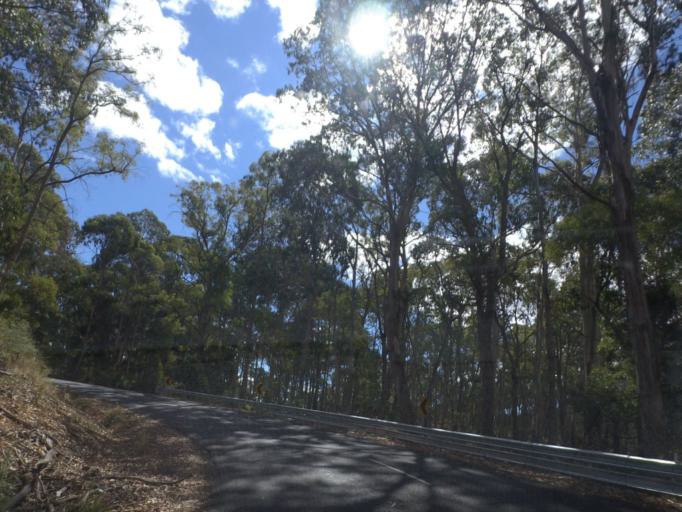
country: AU
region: Victoria
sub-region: Murrindindi
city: Alexandra
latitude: -37.3359
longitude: 145.9620
